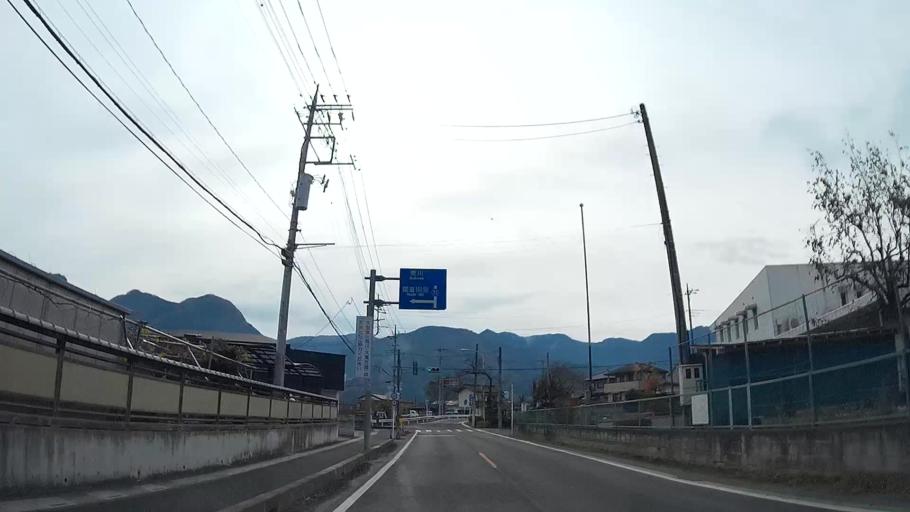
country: JP
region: Saitama
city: Chichibu
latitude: 35.9726
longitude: 139.0528
